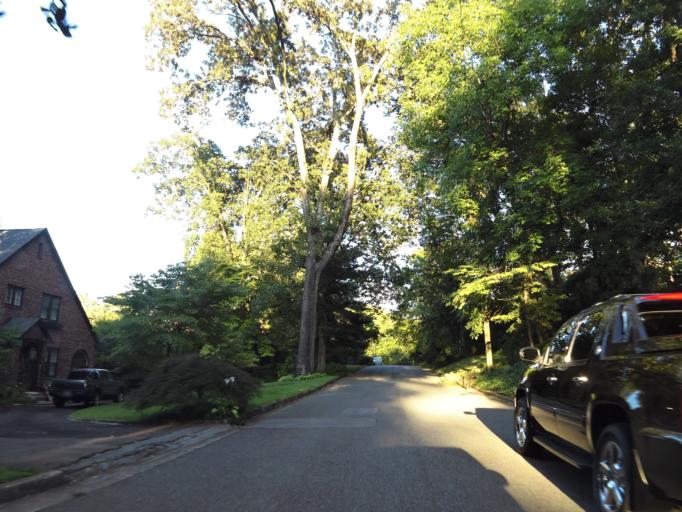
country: US
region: Tennessee
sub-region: Knox County
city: Knoxville
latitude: 35.9391
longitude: -83.9670
